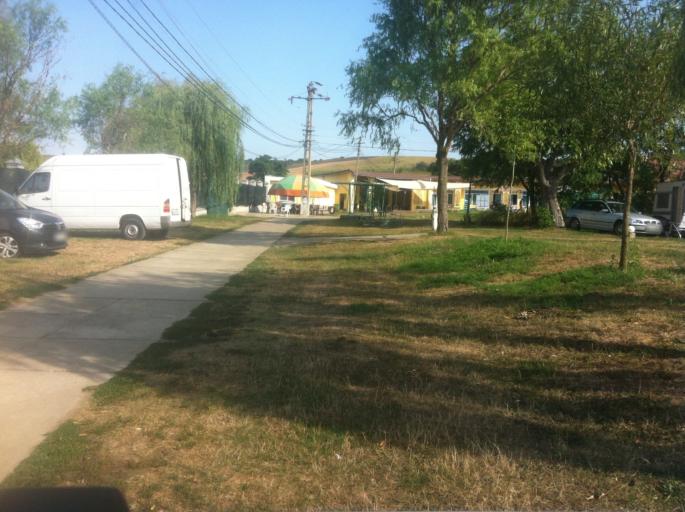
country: RO
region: Sibiu
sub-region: Oras Miercurea Sibiului
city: Miercurea Sibiului
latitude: 45.8905
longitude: 23.7662
